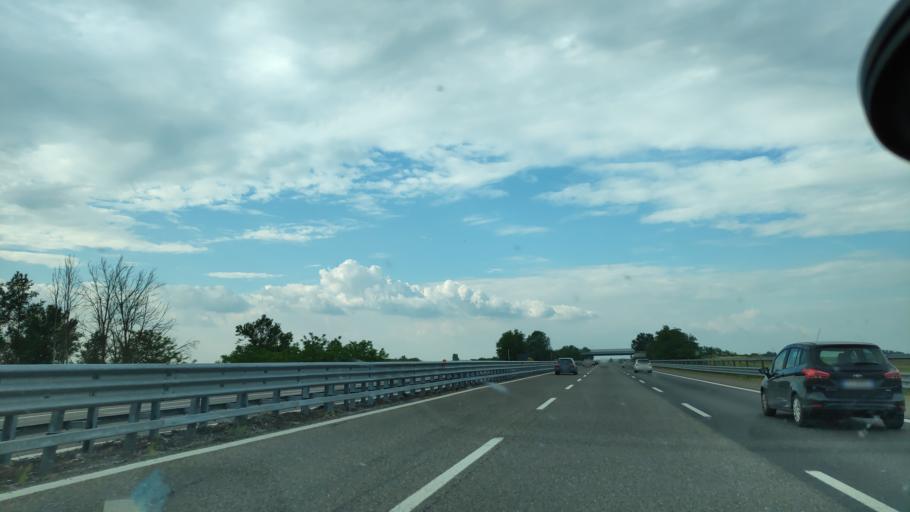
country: IT
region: Lombardy
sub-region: Provincia di Pavia
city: Pieve Albignola
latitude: 45.1213
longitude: 8.9775
